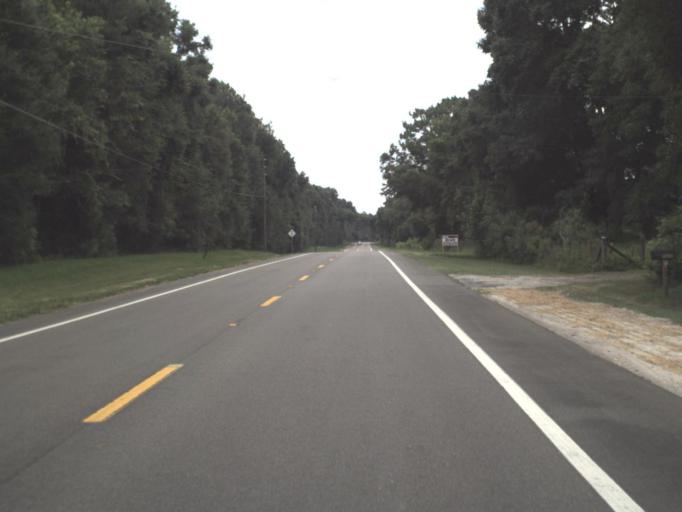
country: US
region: Florida
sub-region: Alachua County
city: Archer
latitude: 29.5118
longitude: -82.5065
